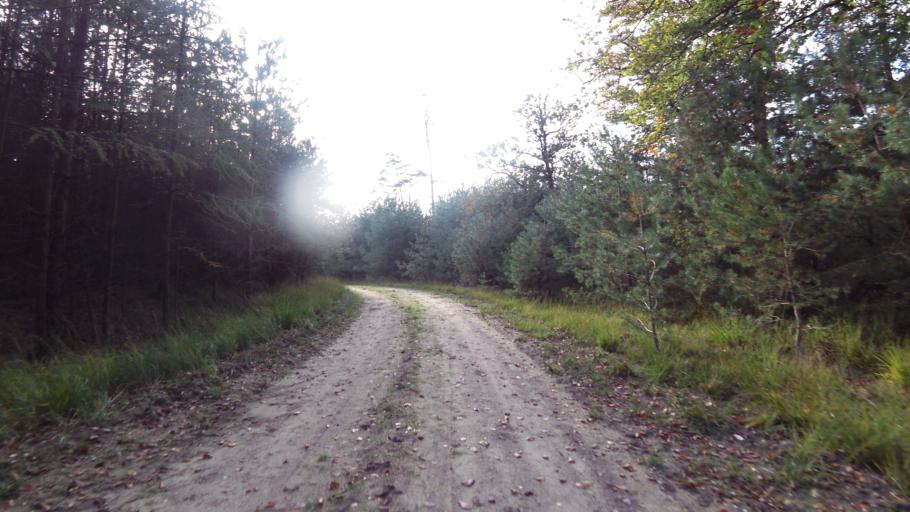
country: NL
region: Gelderland
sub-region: Gemeente Apeldoorn
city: Uddel
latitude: 52.3090
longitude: 5.8431
